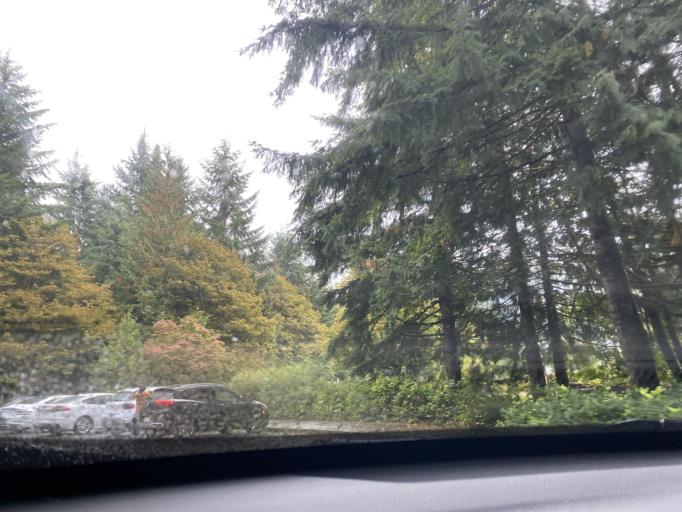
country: CA
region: British Columbia
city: Sooke
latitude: 48.0577
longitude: -123.7893
